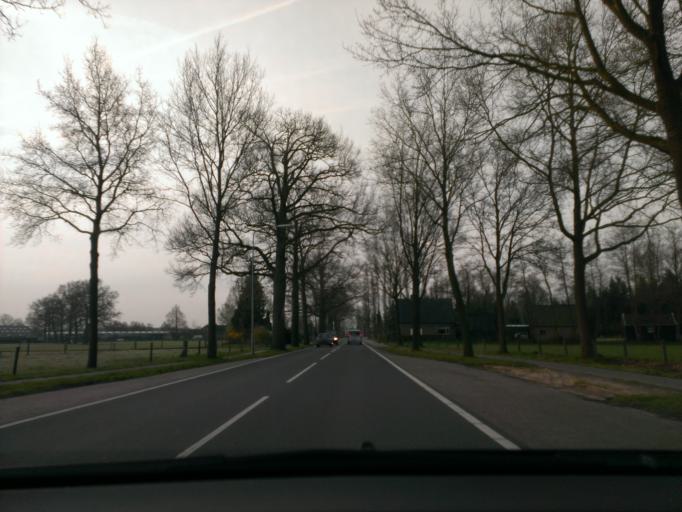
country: NL
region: Gelderland
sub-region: Gemeente Epe
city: Epe
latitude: 52.3347
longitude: 5.9808
